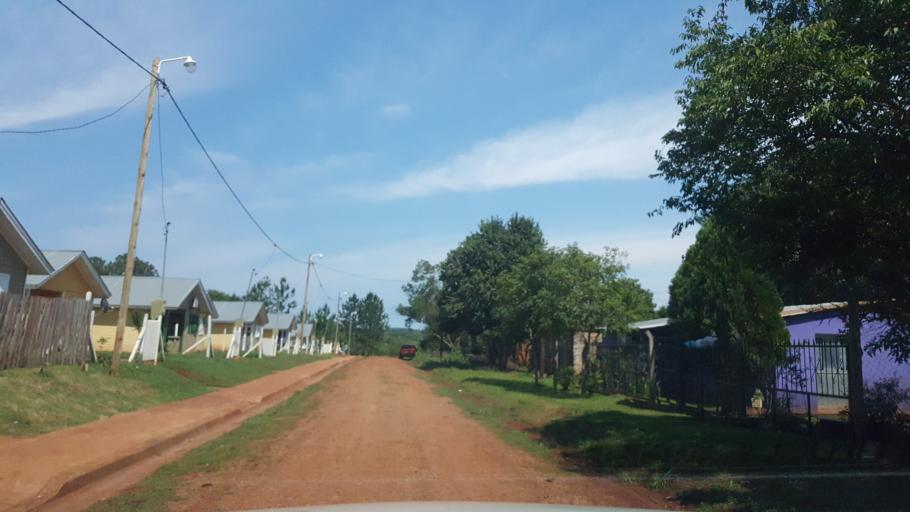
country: AR
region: Misiones
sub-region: Departamento de Apostoles
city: San Jose
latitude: -27.7516
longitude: -55.7924
